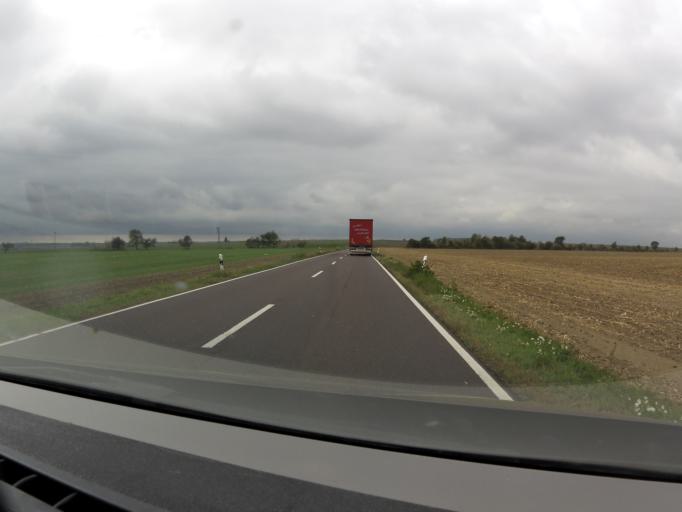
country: DE
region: Saxony-Anhalt
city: Belleben
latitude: 51.6879
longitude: 11.6289
